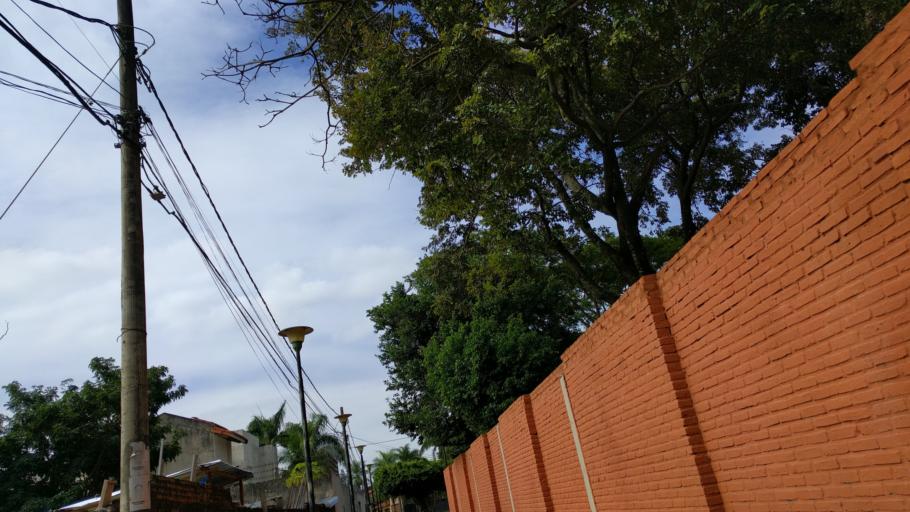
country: BO
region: Santa Cruz
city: Santa Cruz de la Sierra
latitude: -17.8057
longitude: -63.2124
